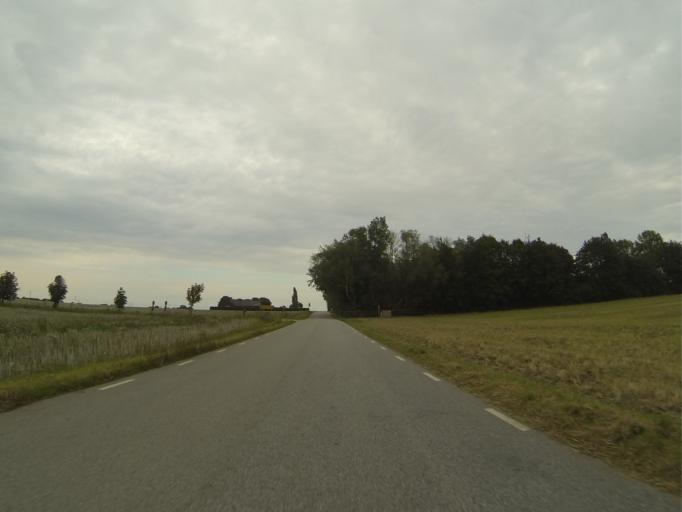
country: SE
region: Skane
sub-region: Staffanstorps Kommun
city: Hjaerup
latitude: 55.6462
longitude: 13.1530
